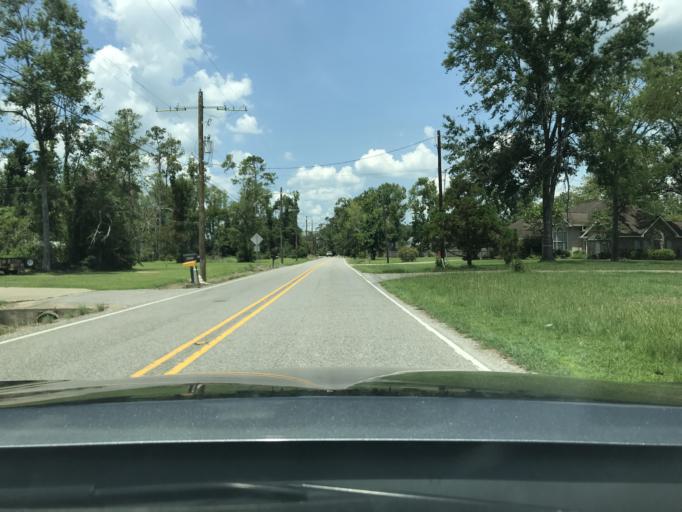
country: US
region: Louisiana
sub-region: Calcasieu Parish
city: Moss Bluff
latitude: 30.3210
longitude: -93.1784
